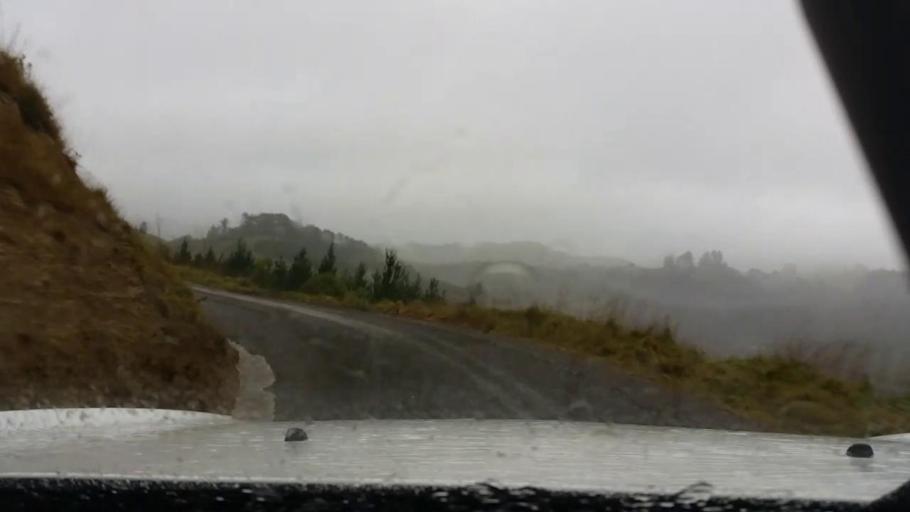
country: NZ
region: Wellington
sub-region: Masterton District
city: Masterton
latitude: -41.1976
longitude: 175.8112
